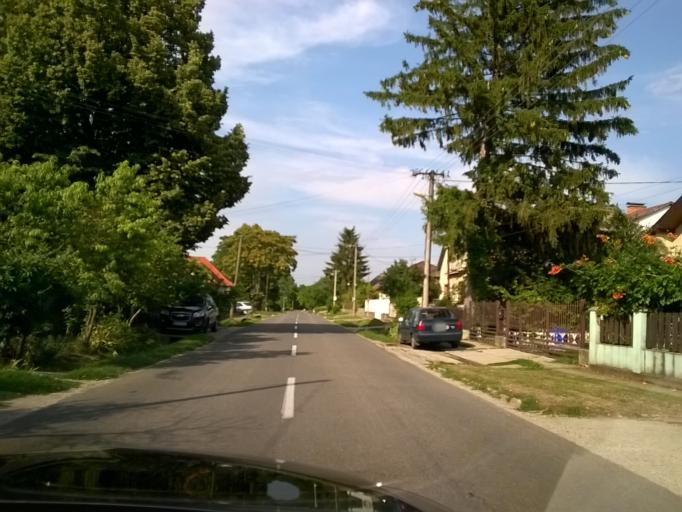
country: SK
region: Trnavsky
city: Hlohovec
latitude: 48.3612
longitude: 17.9374
